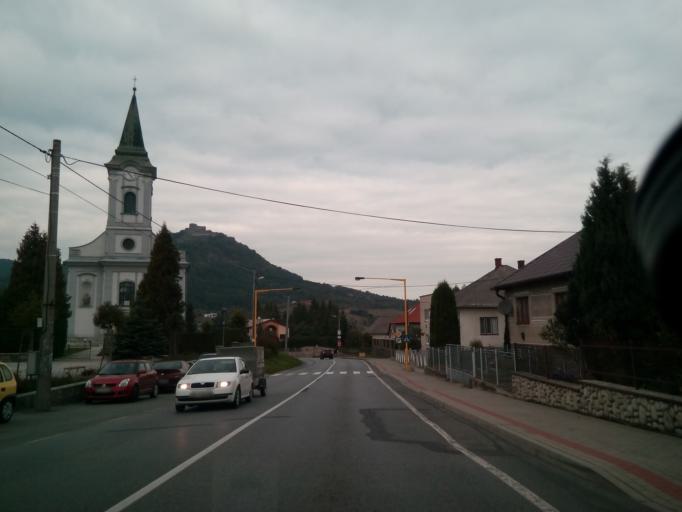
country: SK
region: Presovsky
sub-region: Okres Presov
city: Presov
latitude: 49.0452
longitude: 21.3320
